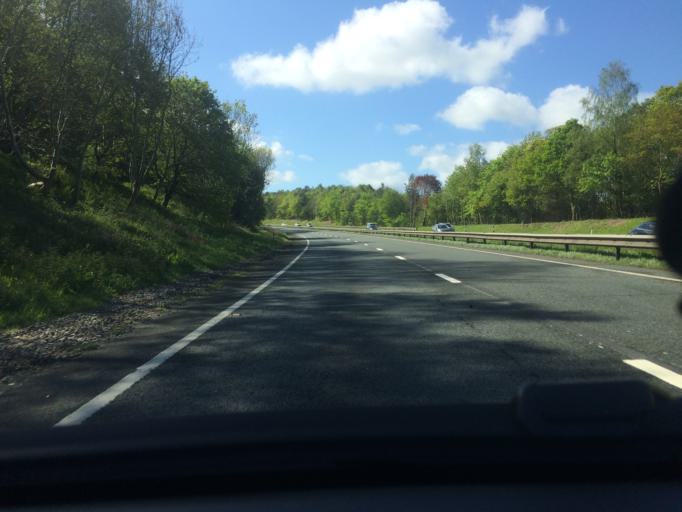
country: GB
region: Wales
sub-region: Wrexham
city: Gresford
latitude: 53.0869
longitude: -2.9864
